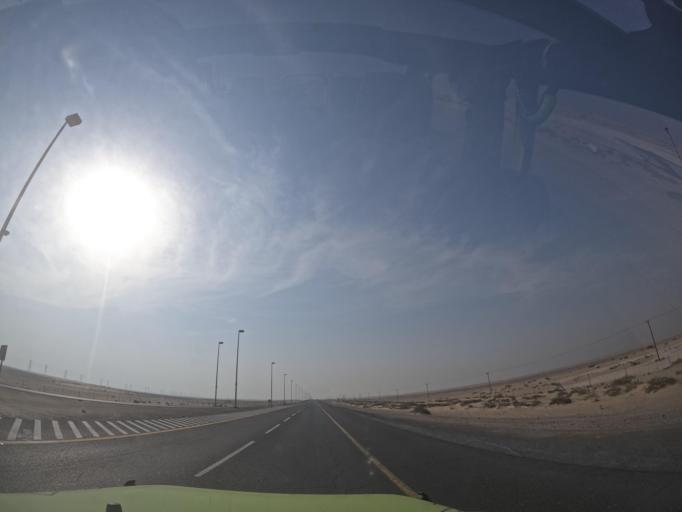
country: AE
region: Dubai
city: Dubai
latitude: 24.7652
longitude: 55.0950
